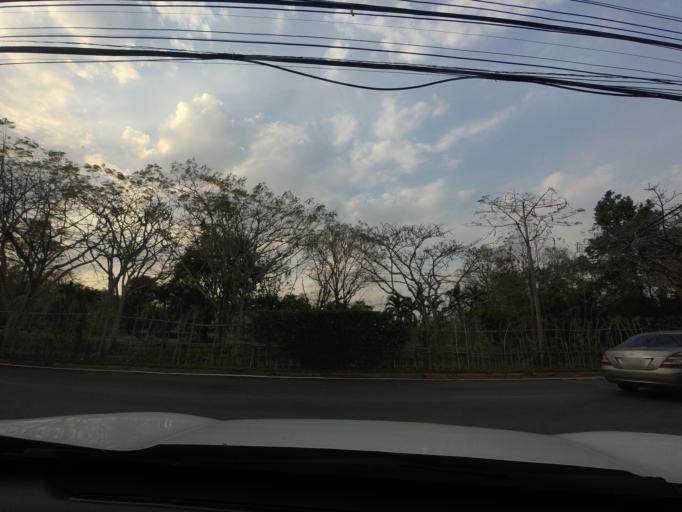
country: TH
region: Nakhon Ratchasima
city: Pak Chong
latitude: 14.5889
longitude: 101.4439
